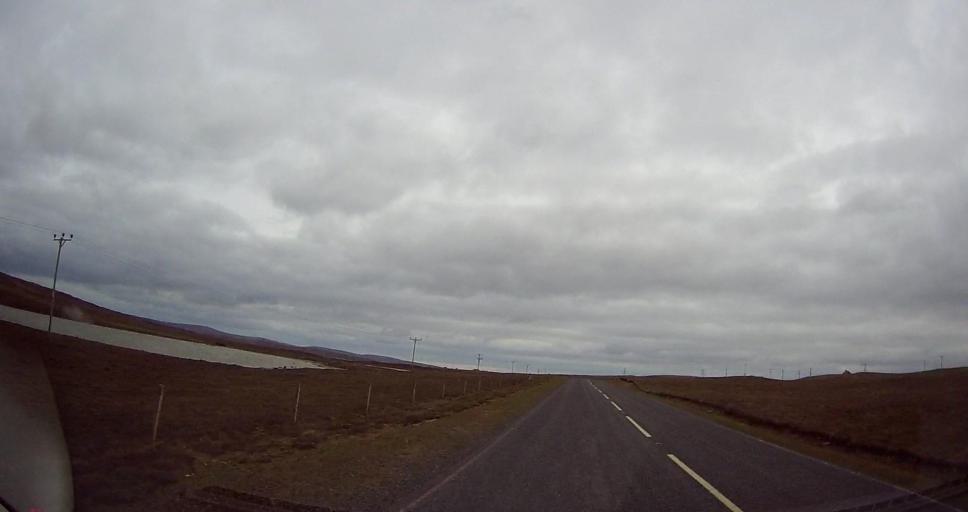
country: GB
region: Scotland
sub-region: Shetland Islands
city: Shetland
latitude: 60.7149
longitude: -0.9147
